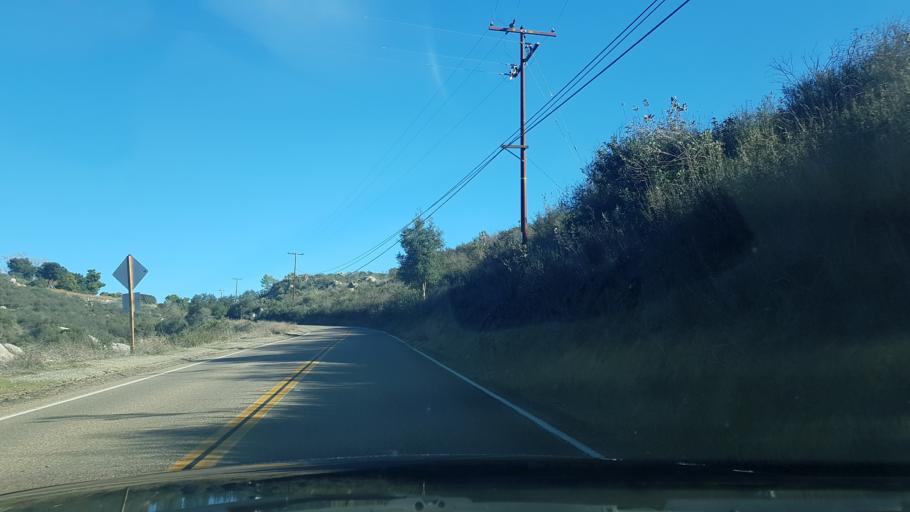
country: US
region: California
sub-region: San Diego County
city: Valley Center
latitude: 33.2000
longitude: -116.9618
